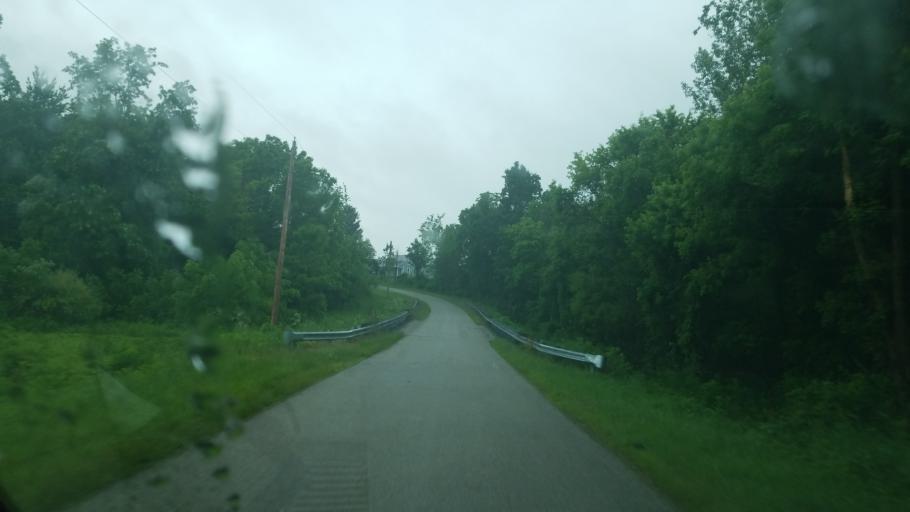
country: US
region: Ohio
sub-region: Huron County
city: Willard
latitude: 40.9440
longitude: -82.7847
